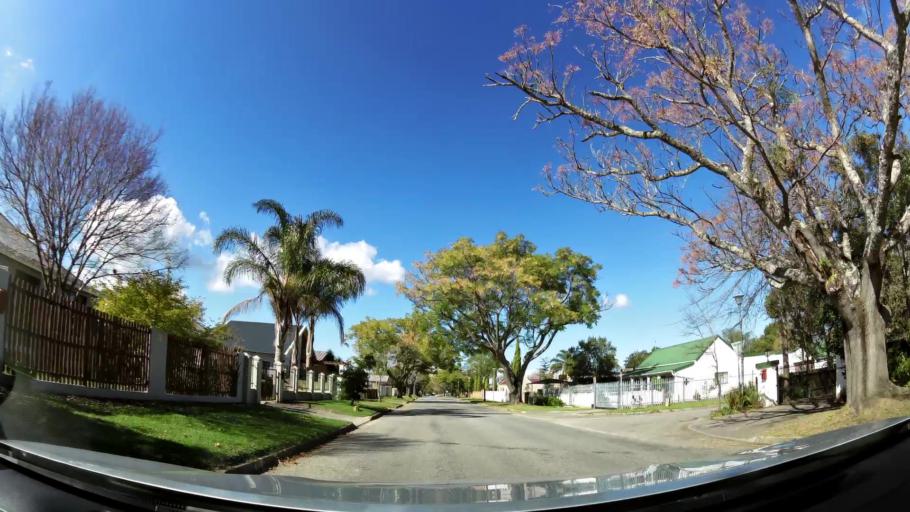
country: ZA
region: Western Cape
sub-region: Eden District Municipality
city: George
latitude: -33.9521
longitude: 22.4651
